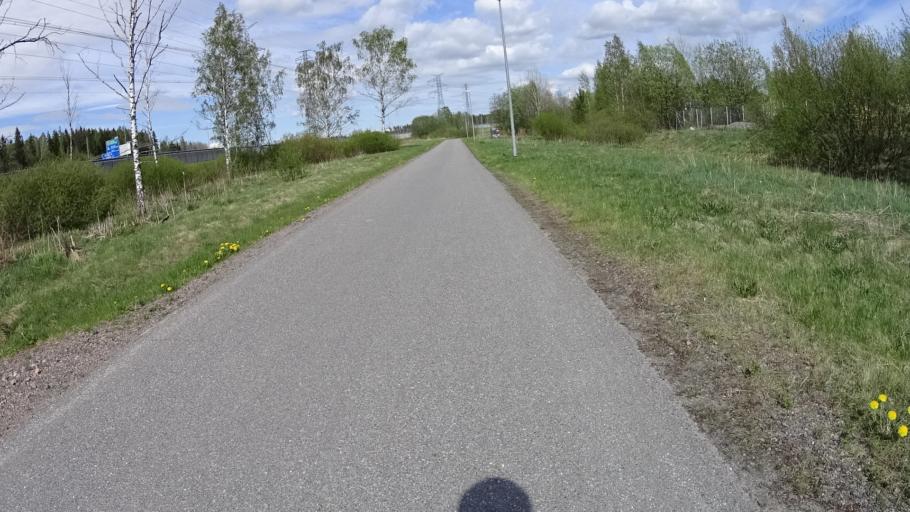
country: FI
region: Uusimaa
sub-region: Helsinki
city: Kilo
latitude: 60.2871
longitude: 24.8365
